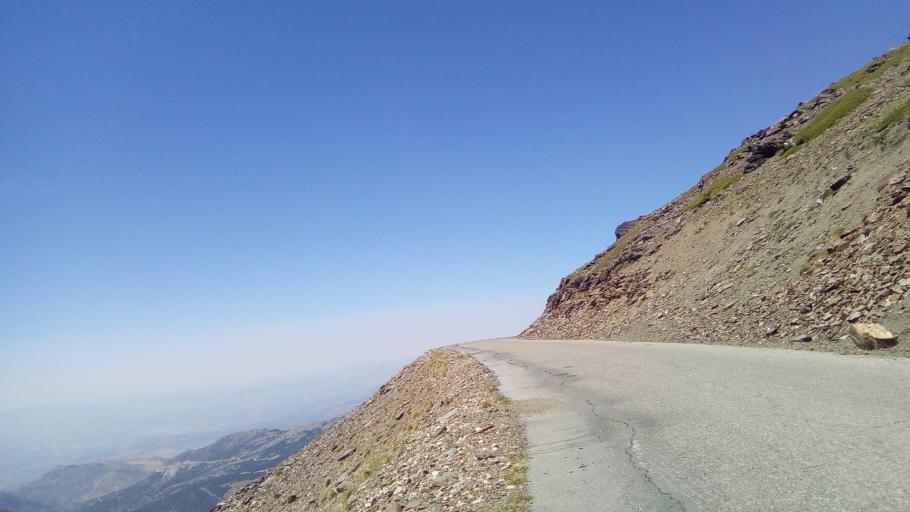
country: ES
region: Andalusia
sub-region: Provincia de Granada
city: Guejar-Sierra
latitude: 37.0749
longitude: -3.3845
